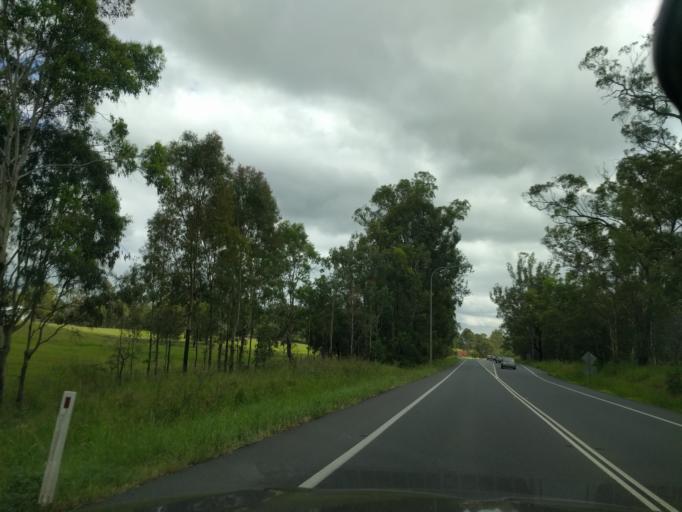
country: AU
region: Queensland
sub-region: Logan
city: Cedar Vale
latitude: -27.8672
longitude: 152.9992
